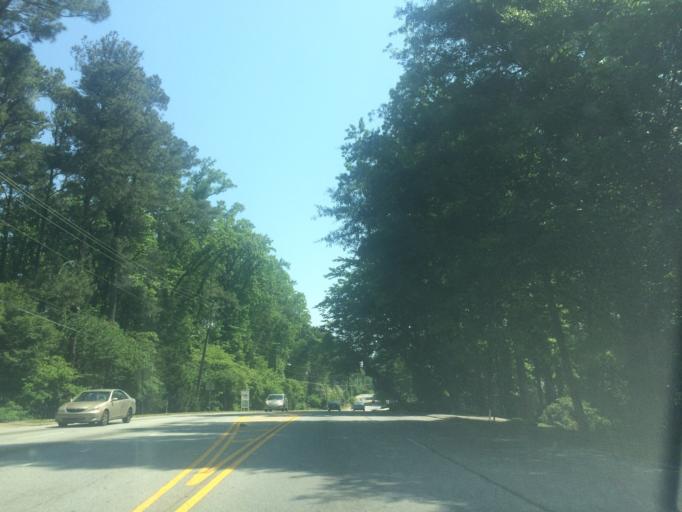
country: US
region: Georgia
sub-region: DeKalb County
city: North Decatur
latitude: 33.7851
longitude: -84.3037
